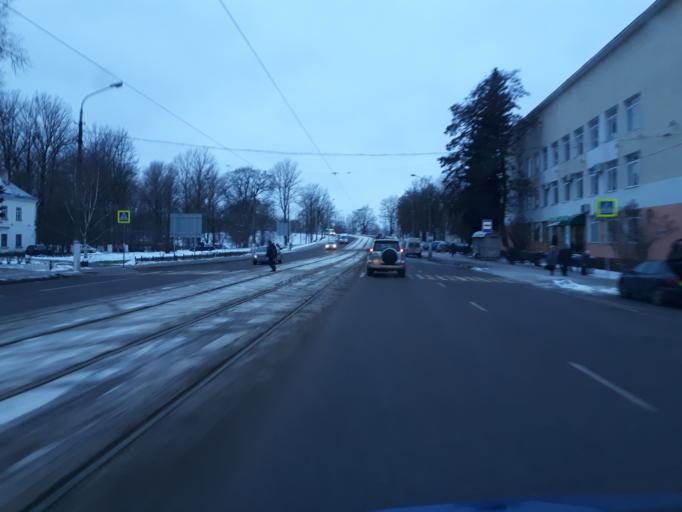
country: BY
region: Vitebsk
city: Vitebsk
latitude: 55.1733
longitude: 30.1504
